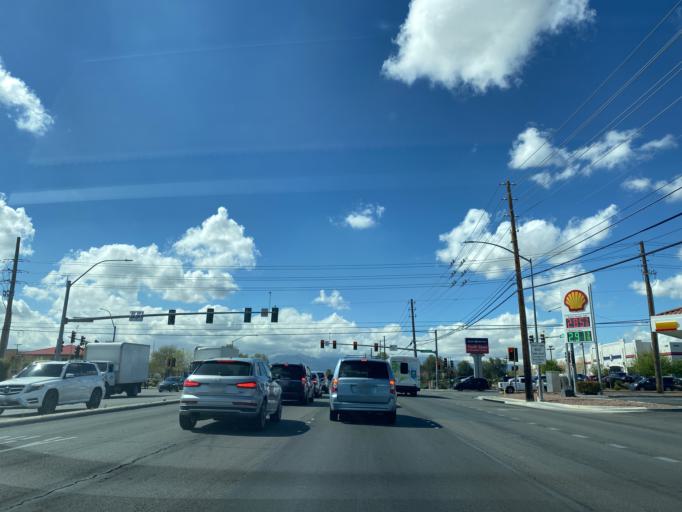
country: US
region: Nevada
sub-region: Clark County
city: North Las Vegas
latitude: 36.2395
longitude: -115.1886
